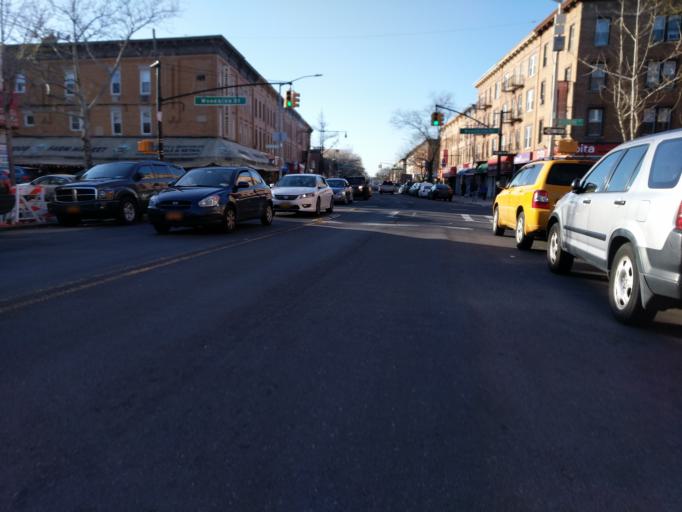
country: US
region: New York
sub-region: Kings County
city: East New York
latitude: 40.7071
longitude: -73.8973
